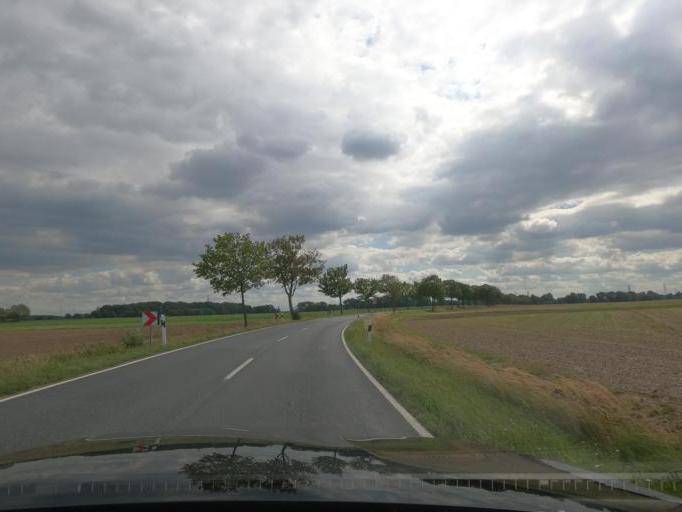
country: DE
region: Lower Saxony
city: Lehrte
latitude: 52.3525
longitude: 10.0272
